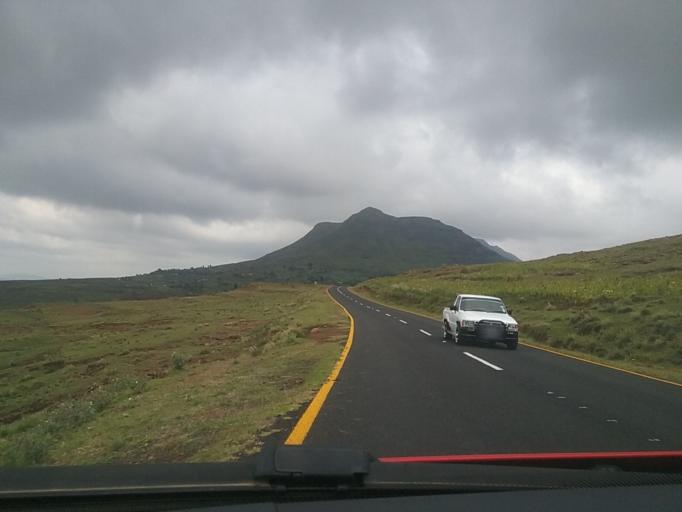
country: LS
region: Berea
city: Teyateyaneng
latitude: -29.2436
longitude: 27.8560
